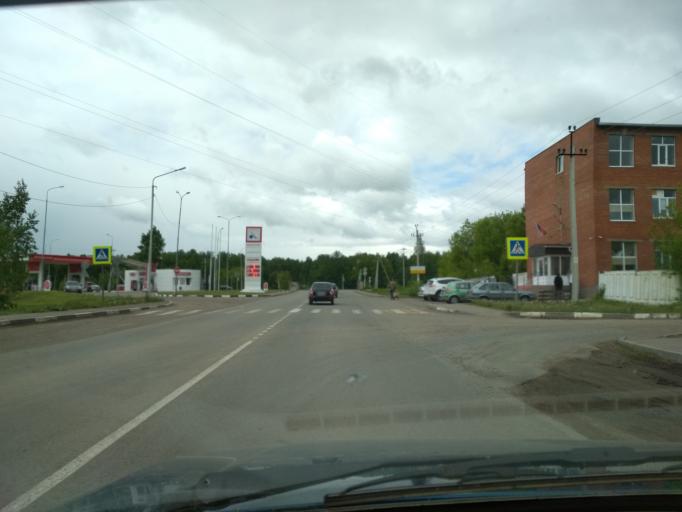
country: RU
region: Tatarstan
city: Zainsk
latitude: 55.2980
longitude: 51.9917
